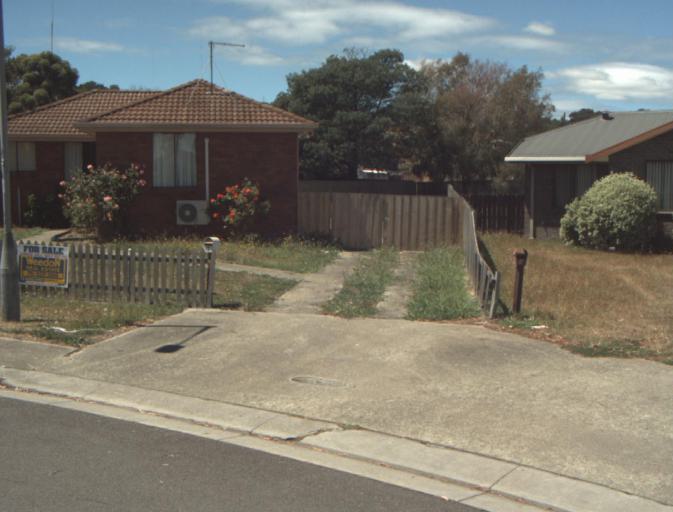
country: AU
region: Tasmania
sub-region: Launceston
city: Mayfield
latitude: -41.3808
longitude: 147.1328
